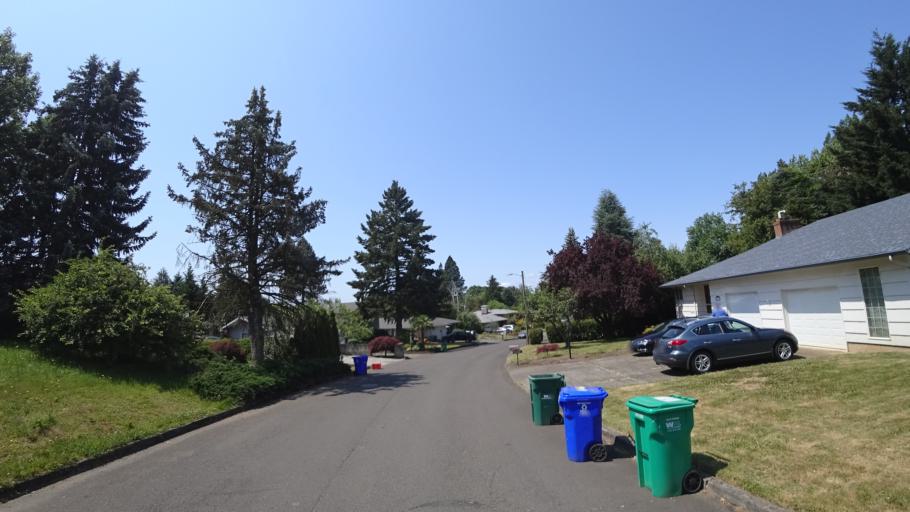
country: US
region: Oregon
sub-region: Multnomah County
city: Lents
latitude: 45.4452
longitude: -122.5734
